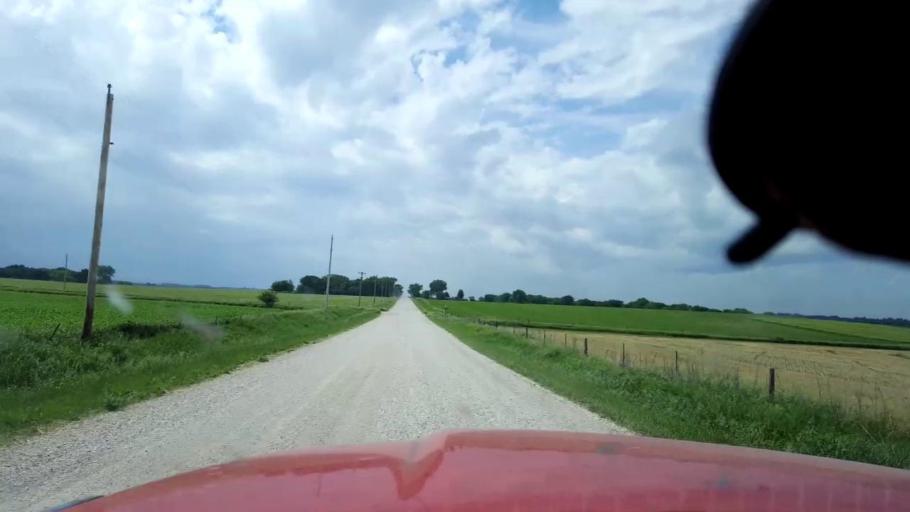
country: US
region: Iowa
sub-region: Cherokee County
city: Cherokee
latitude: 42.8157
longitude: -95.5346
